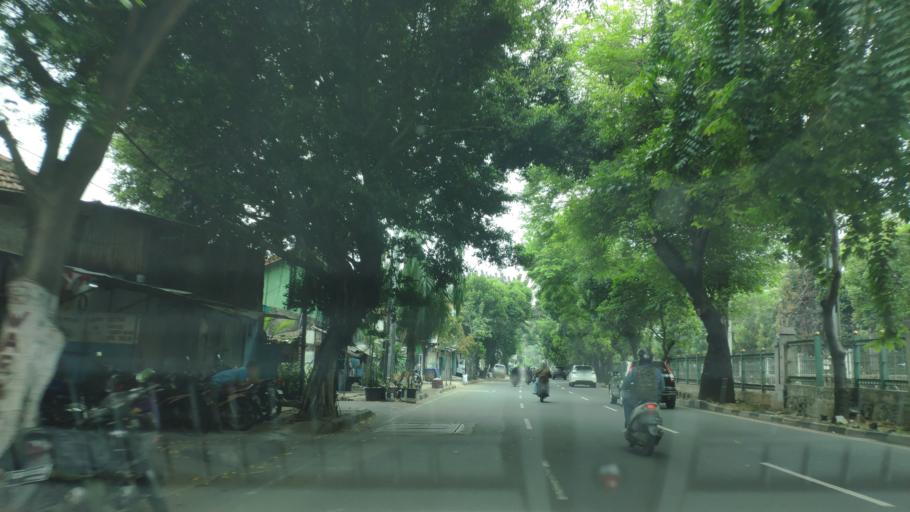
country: ID
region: Jakarta Raya
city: Jakarta
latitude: -6.2156
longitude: 106.7939
